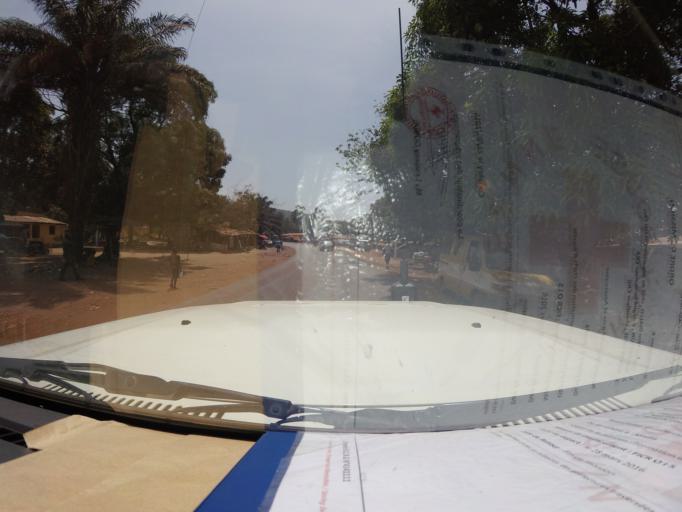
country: GN
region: Kindia
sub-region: Coyah
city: Coyah
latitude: 9.7783
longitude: -13.3443
